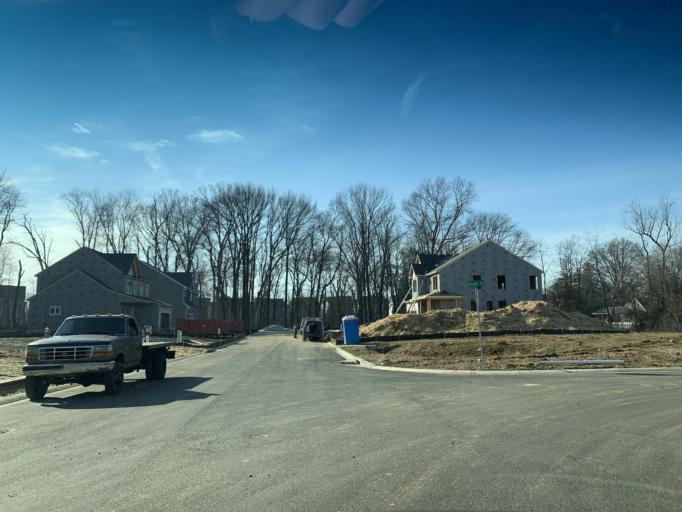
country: US
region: Maryland
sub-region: Harford County
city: Pleasant Hills
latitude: 39.5000
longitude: -76.3908
